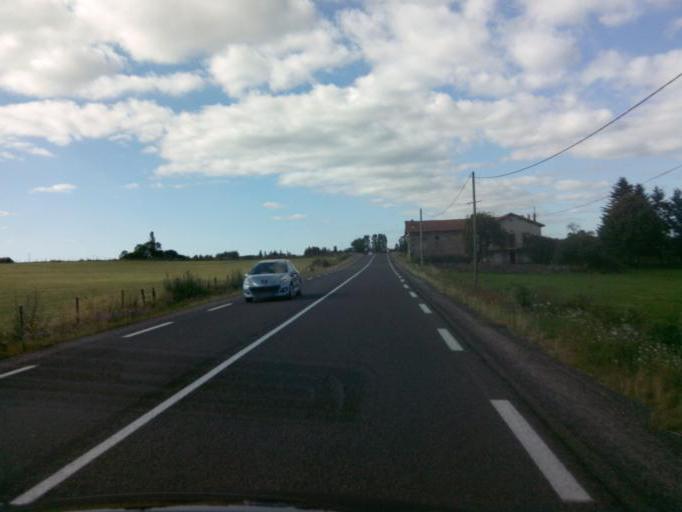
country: FR
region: Auvergne
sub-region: Departement de la Haute-Loire
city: Saint-Paulien
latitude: 45.1914
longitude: 3.8227
